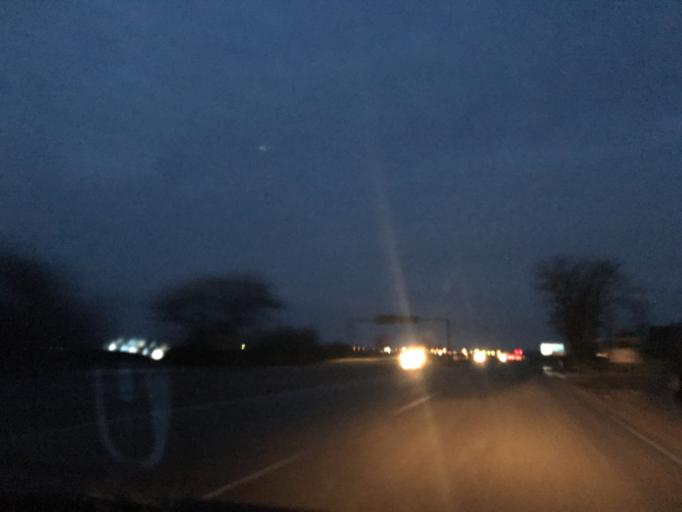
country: RU
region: Rostov
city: Bataysk
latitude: 47.0772
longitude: 39.7638
